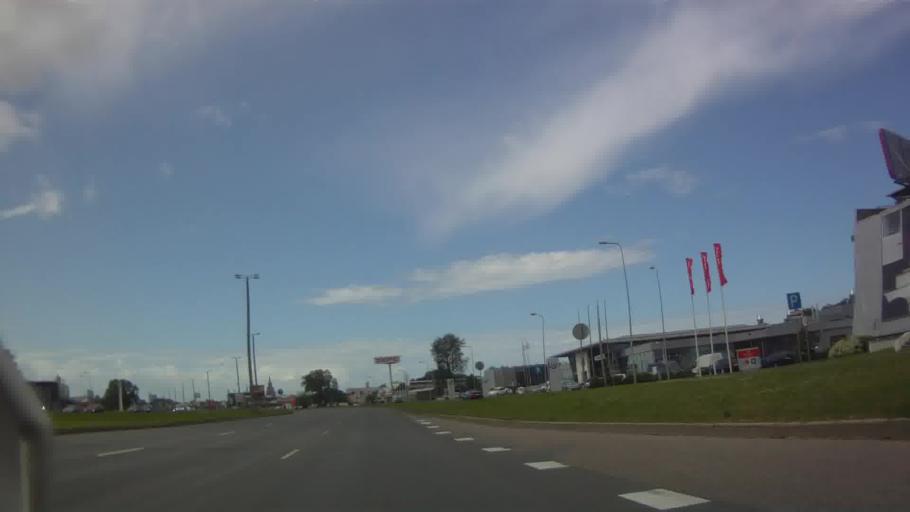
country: LV
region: Riga
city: Riga
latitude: 56.9310
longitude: 24.1514
